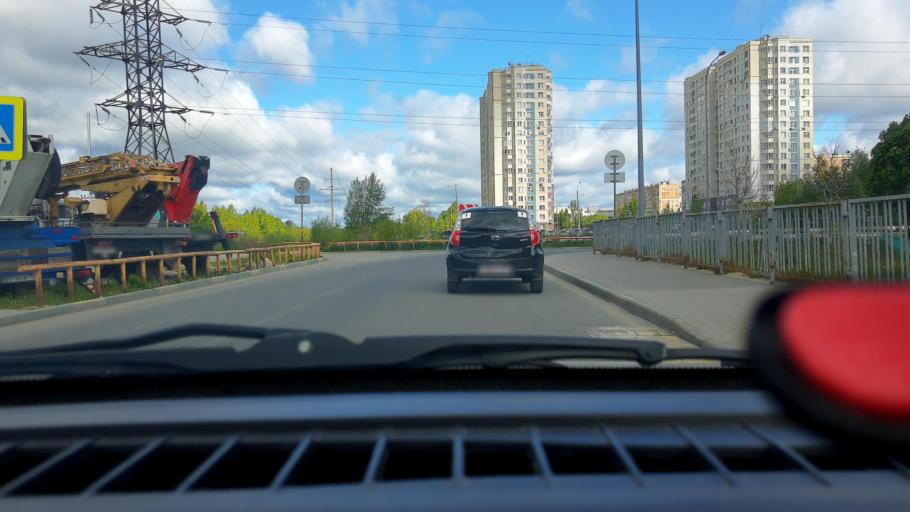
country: RU
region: Nizjnij Novgorod
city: Burevestnik
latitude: 56.2167
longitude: 43.8581
